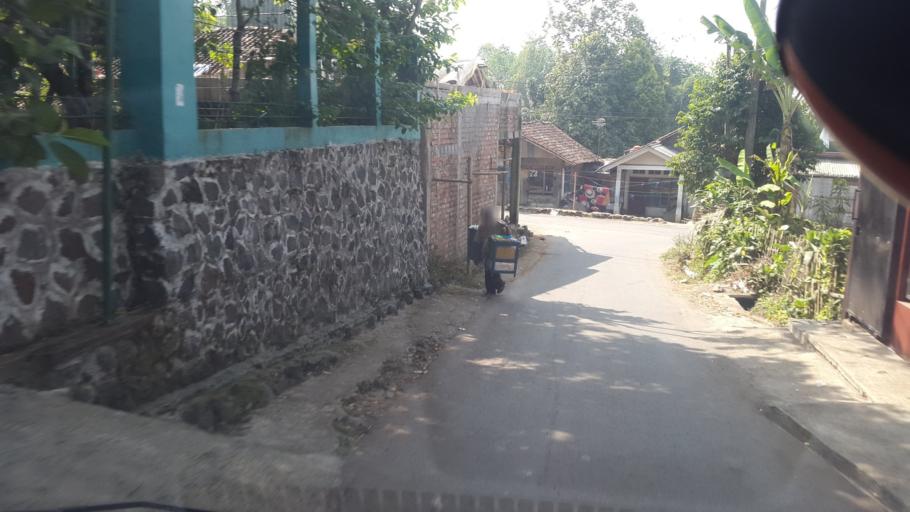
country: ID
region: West Java
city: Sukabumi
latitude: -6.8862
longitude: 106.9139
